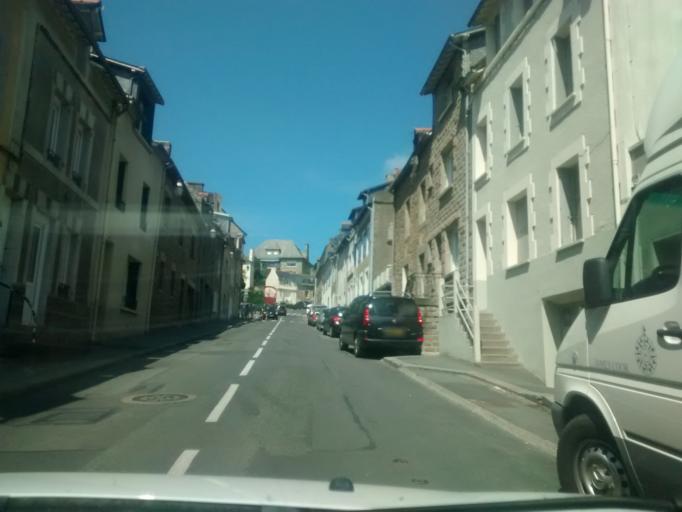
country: FR
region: Brittany
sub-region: Departement d'Ille-et-Vilaine
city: Cancale
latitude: 48.6724
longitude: -1.8530
